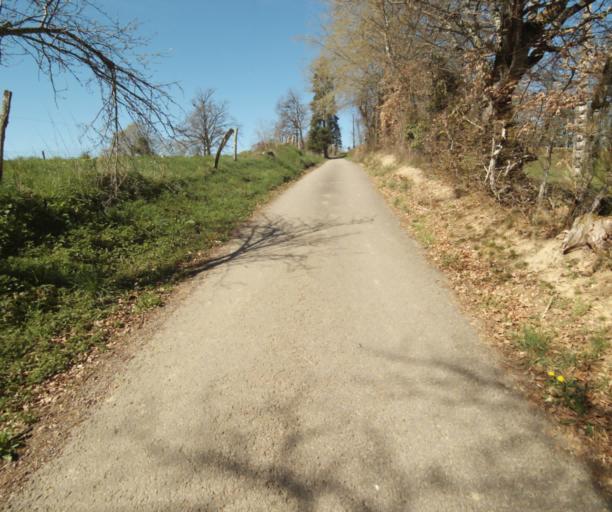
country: FR
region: Limousin
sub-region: Departement de la Correze
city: Saint-Mexant
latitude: 45.3080
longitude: 1.6440
